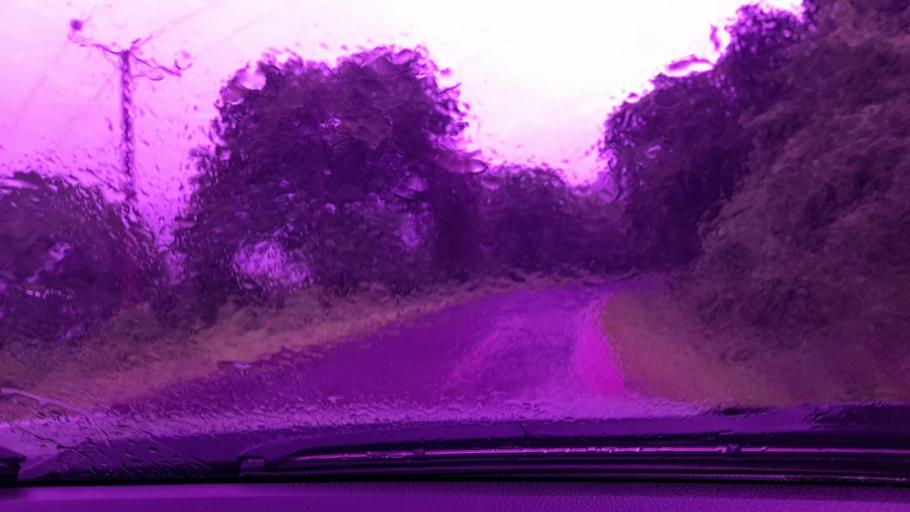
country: ET
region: Oromiya
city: Metu
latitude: 8.4754
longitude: 35.6392
